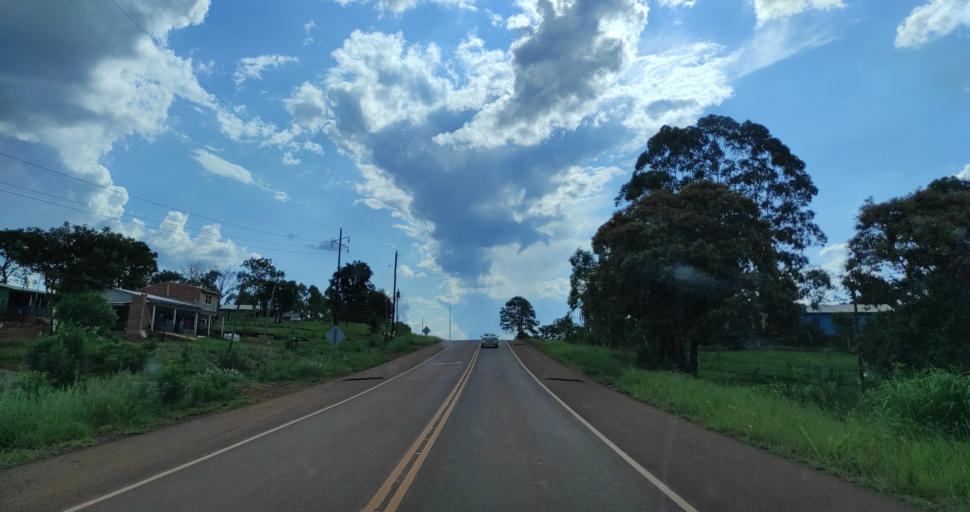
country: AR
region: Misiones
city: Bernardo de Irigoyen
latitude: -26.2931
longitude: -53.7706
